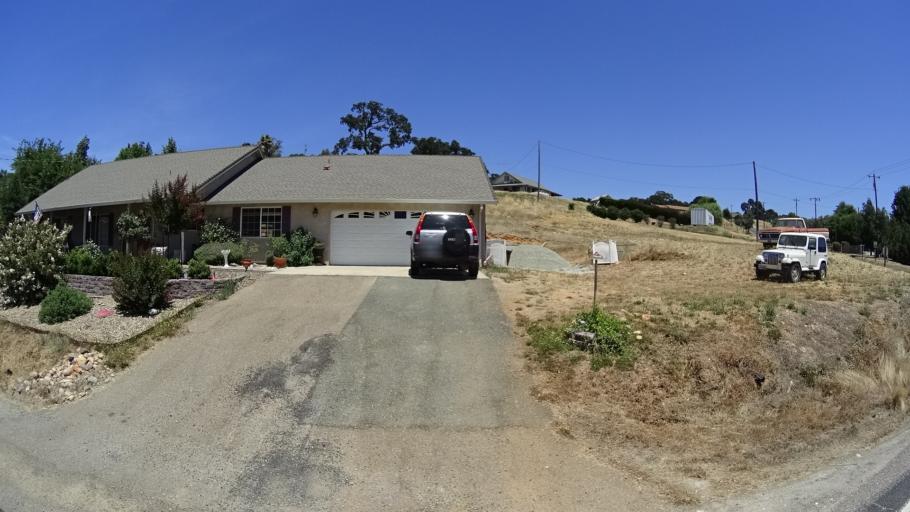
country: US
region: California
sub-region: Calaveras County
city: Rancho Calaveras
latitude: 38.0970
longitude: -120.8745
